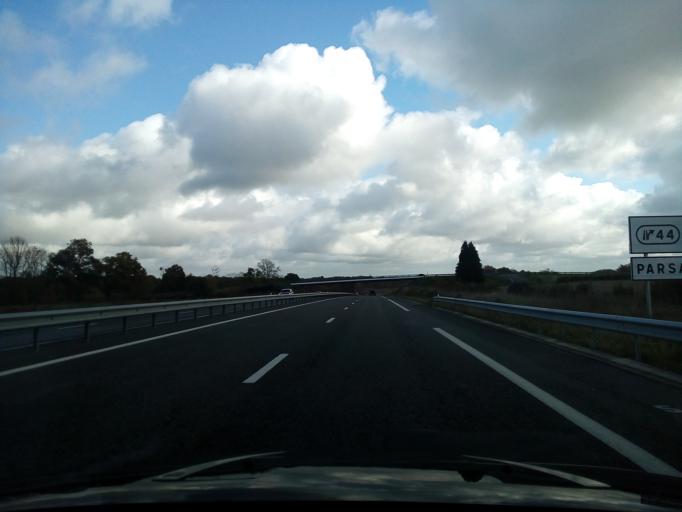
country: FR
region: Limousin
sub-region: Departement de la Creuse
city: Ajain
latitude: 46.2047
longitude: 2.0828
